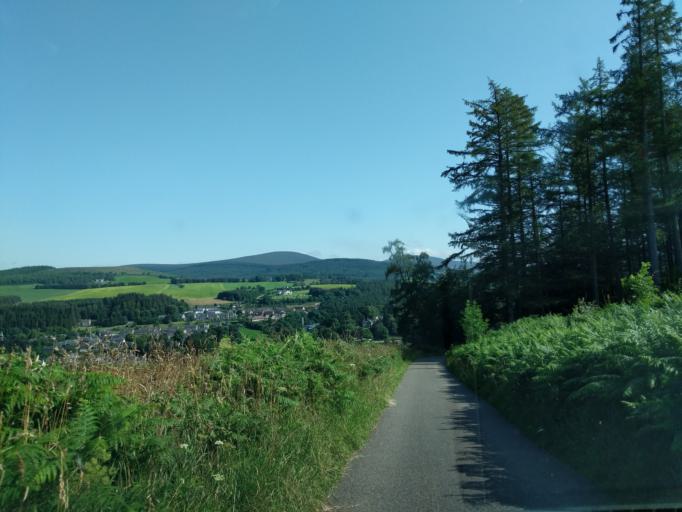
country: GB
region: Scotland
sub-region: Moray
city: Rothes
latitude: 57.4722
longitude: -3.2362
